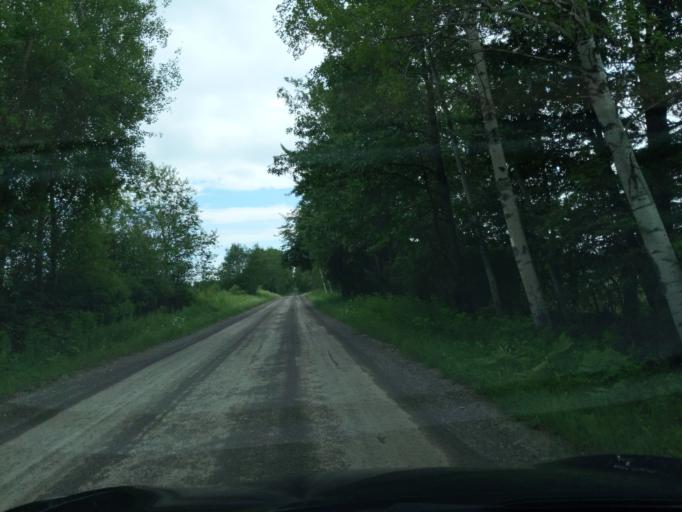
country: US
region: Michigan
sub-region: Clare County
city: Harrison
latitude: 43.9836
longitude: -84.9983
